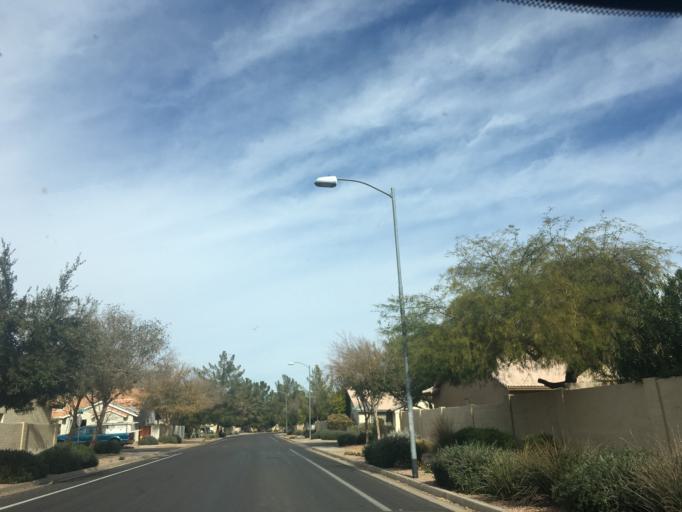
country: US
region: Arizona
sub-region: Maricopa County
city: Gilbert
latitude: 33.3460
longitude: -111.8031
